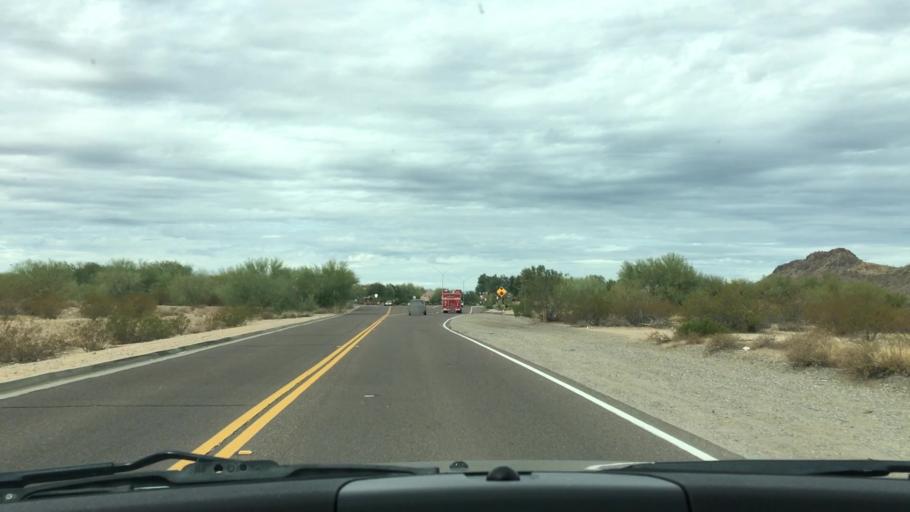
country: US
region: Arizona
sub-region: Maricopa County
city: Sun City West
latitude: 33.7226
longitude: -112.2374
